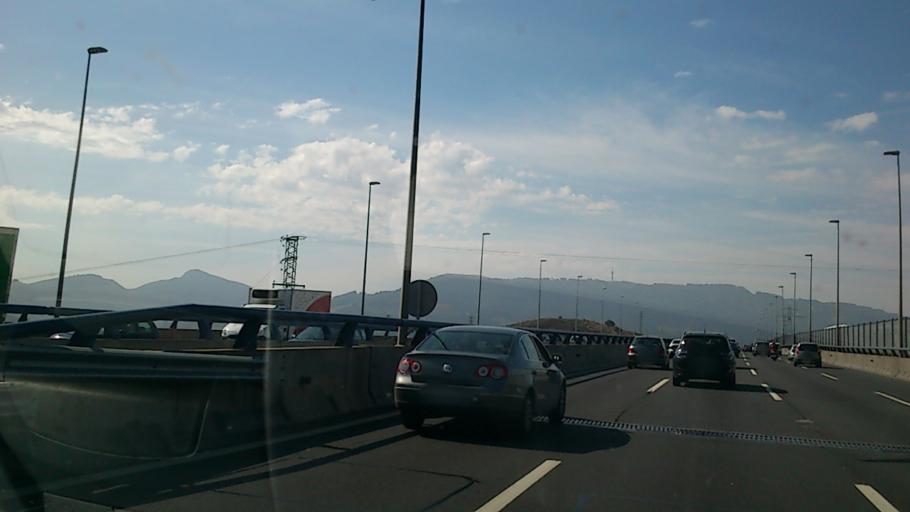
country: ES
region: Basque Country
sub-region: Bizkaia
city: Barakaldo
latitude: 43.2961
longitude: -2.9698
